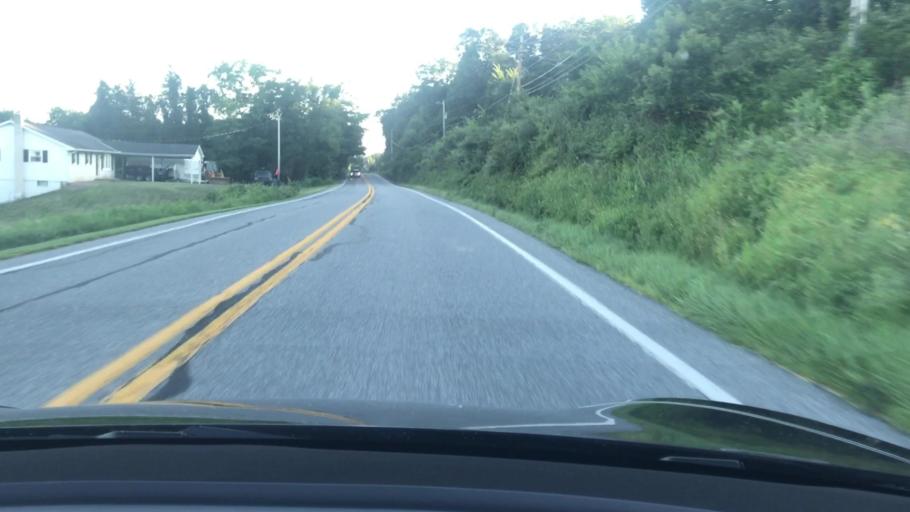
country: US
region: Pennsylvania
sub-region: York County
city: Dover
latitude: 40.0588
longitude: -76.8879
